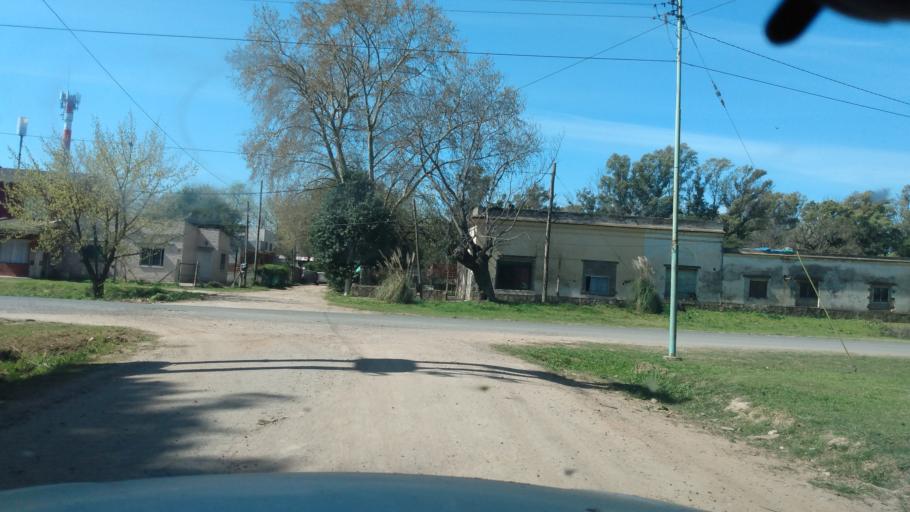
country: AR
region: Buenos Aires
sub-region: Partido de Lujan
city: Lujan
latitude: -34.5724
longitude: -59.1301
